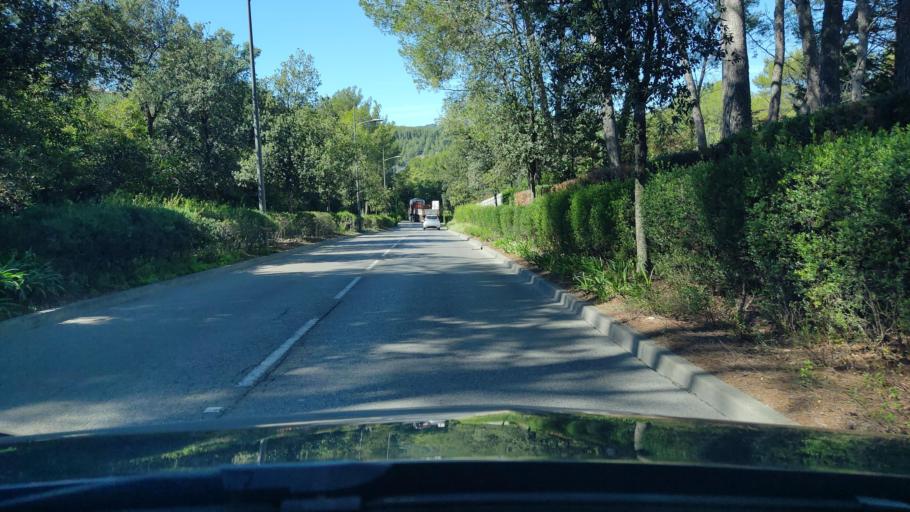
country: FR
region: Provence-Alpes-Cote d'Azur
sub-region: Departement du Var
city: Sanary-sur-Mer
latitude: 43.1438
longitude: 5.7736
